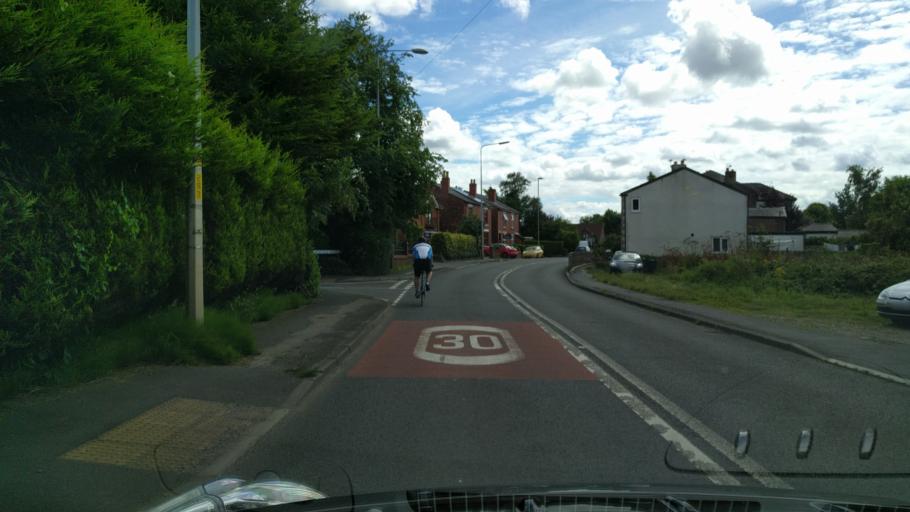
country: GB
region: England
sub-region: Borough of Wigan
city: Leigh
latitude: 53.4725
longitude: -2.4952
